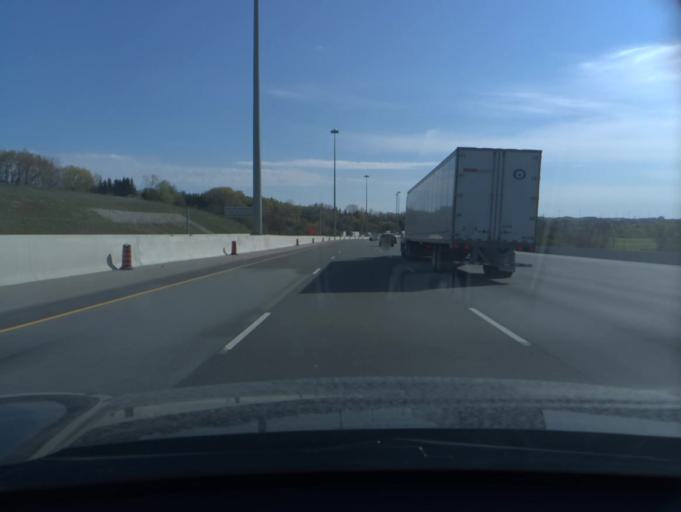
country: CA
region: Ontario
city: North Perth
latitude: 43.8200
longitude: -80.9999
